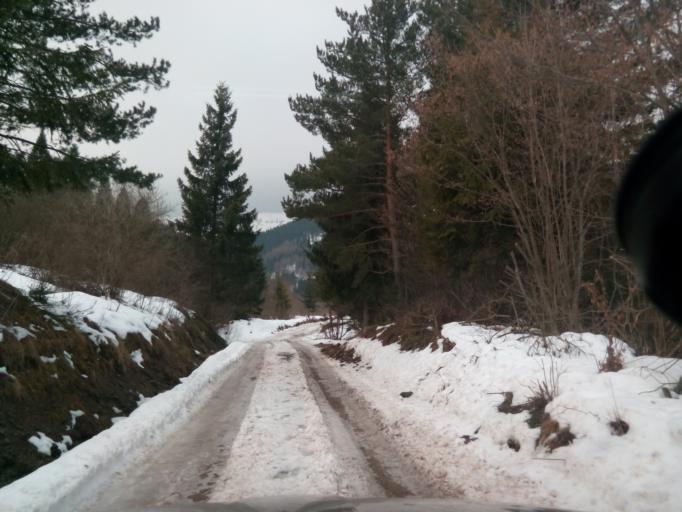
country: SK
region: Presovsky
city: Stara L'ubovna
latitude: 49.2139
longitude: 20.7471
